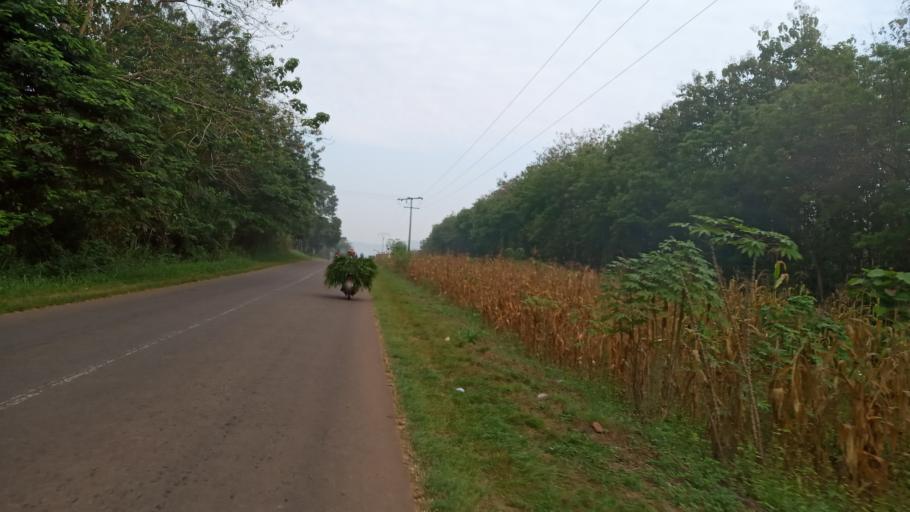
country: TG
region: Plateaux
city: Kpalime
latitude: 6.8861
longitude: 0.6446
